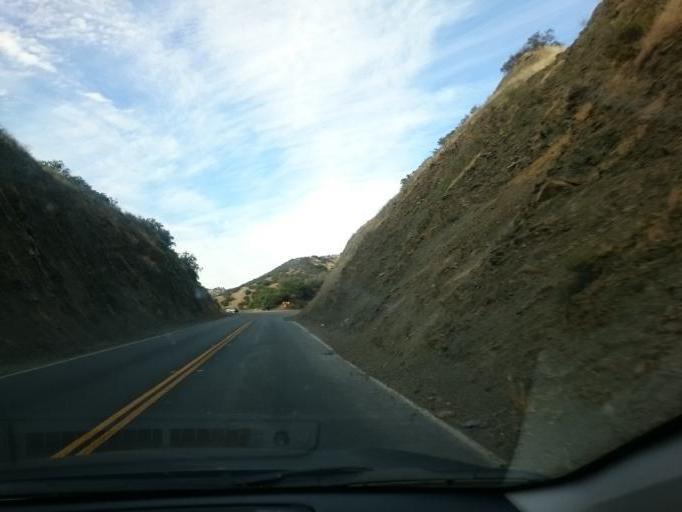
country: US
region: California
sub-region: Yolo County
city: Winters
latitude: 38.5045
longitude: -122.1158
